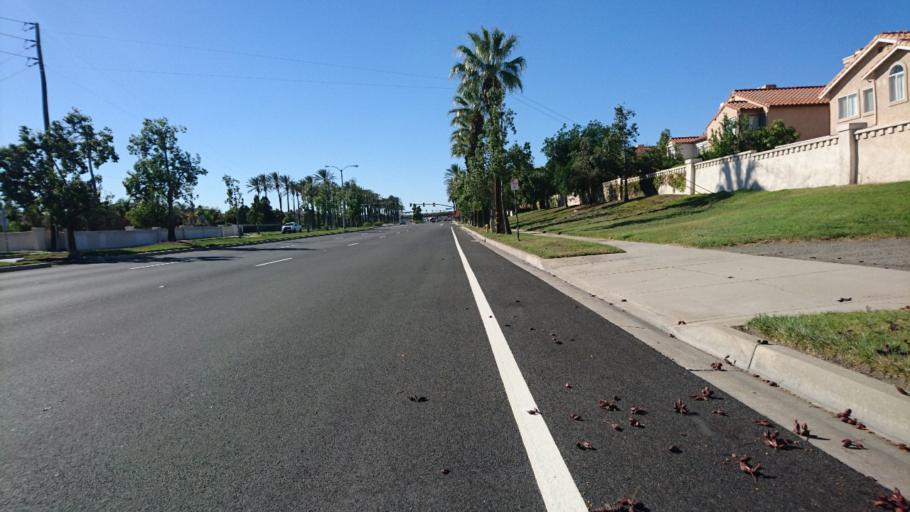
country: US
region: California
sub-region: San Bernardino County
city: Fontana
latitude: 34.1216
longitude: -117.5061
